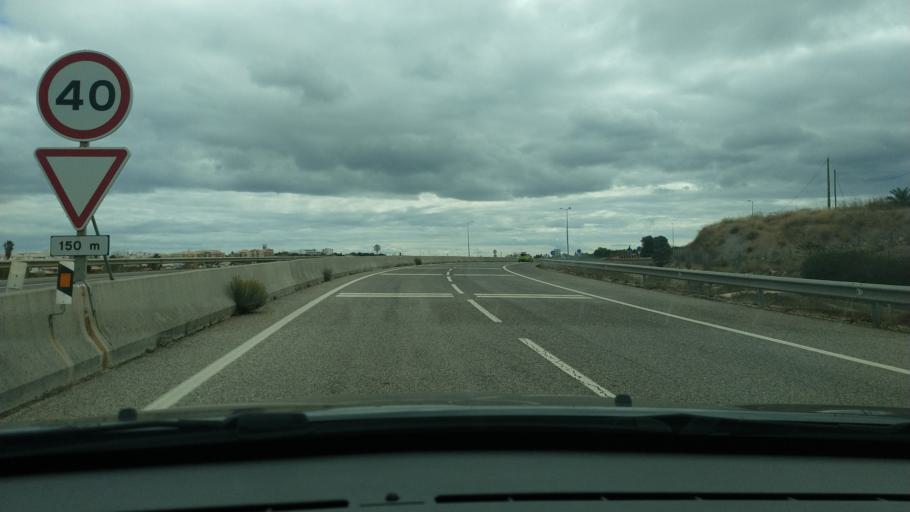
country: PT
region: Faro
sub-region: Lagos
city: Lagos
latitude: 37.1036
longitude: -8.6953
